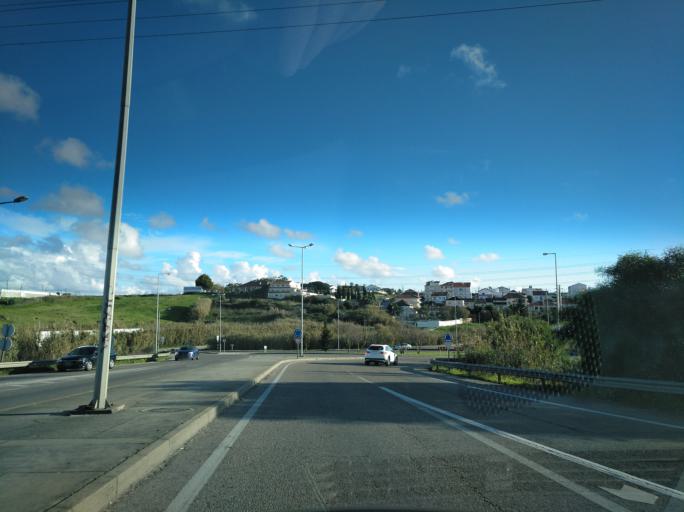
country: PT
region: Setubal
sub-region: Almada
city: Sobreda
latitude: 38.6599
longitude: -9.1884
